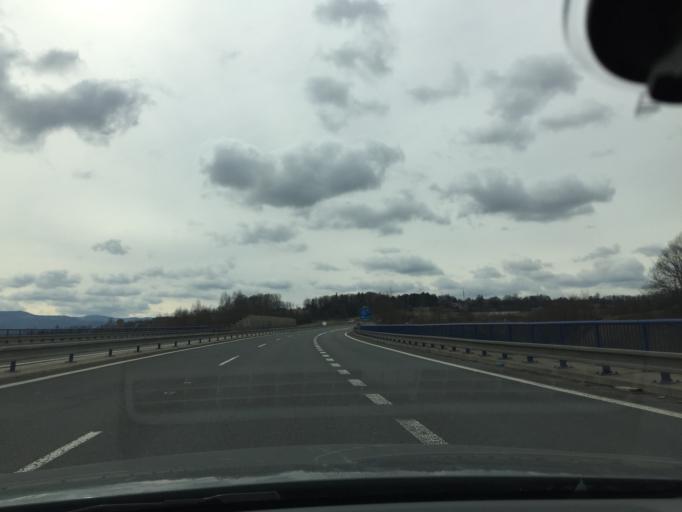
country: CZ
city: Ropice
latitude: 49.7302
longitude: 18.6053
